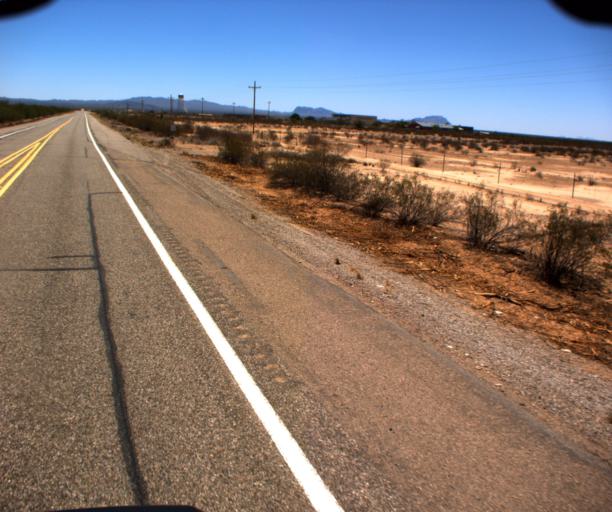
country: US
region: Arizona
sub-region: Pima County
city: Ajo
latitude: 32.1903
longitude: -112.4123
